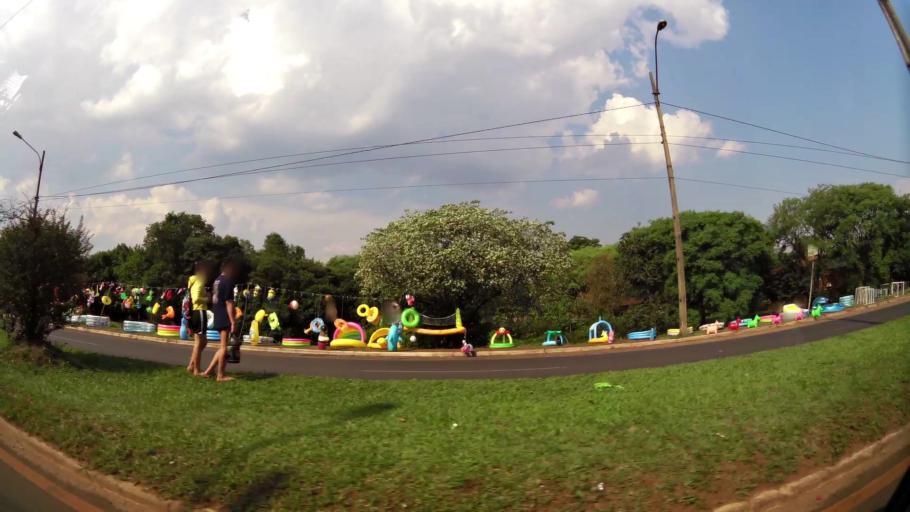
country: PY
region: Alto Parana
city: Presidente Franco
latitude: -25.5273
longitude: -54.6351
